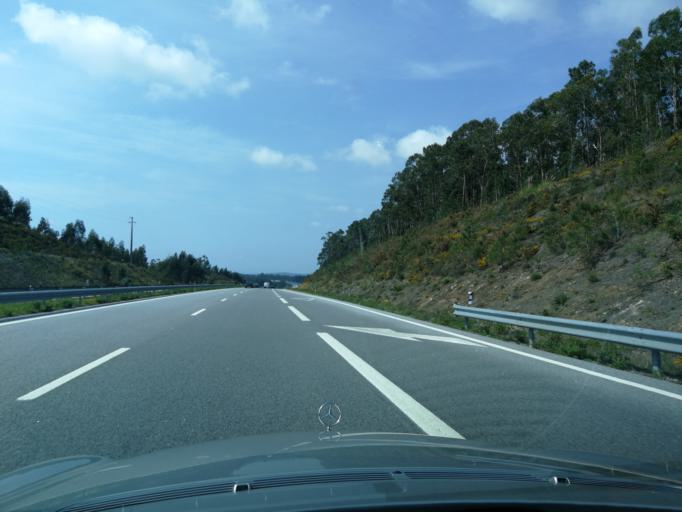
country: PT
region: Braga
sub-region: Vila Nova de Famalicao
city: Ribeirao
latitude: 41.3815
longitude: -8.5756
